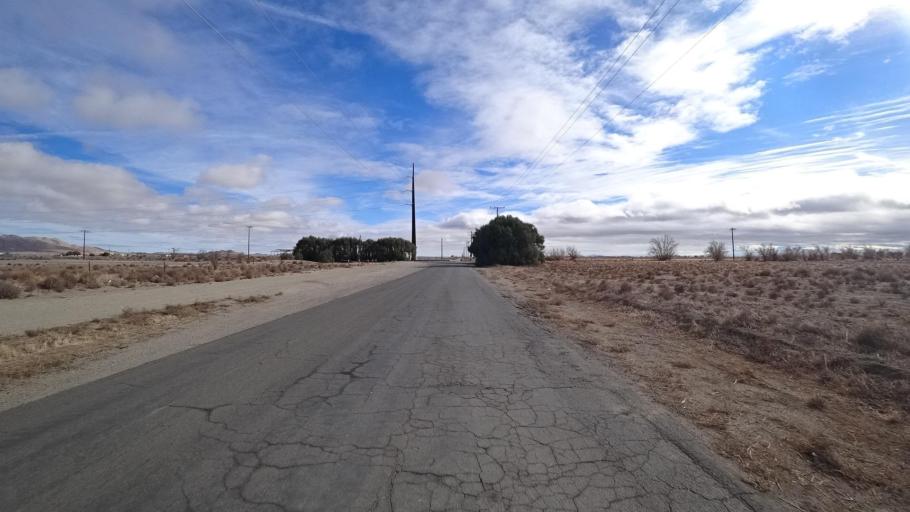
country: US
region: California
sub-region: Kern County
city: Rosamond
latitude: 34.8343
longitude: -118.3098
